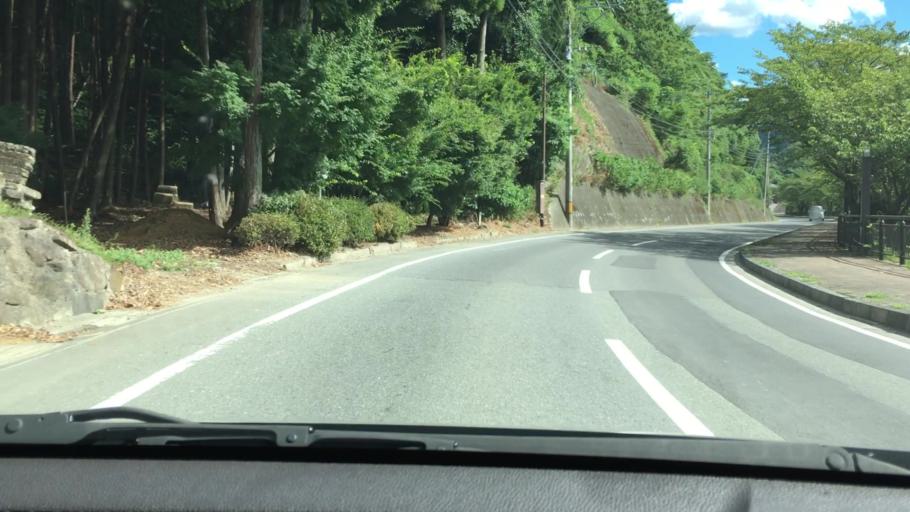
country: JP
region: Saga Prefecture
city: Takeocho-takeo
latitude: 33.1813
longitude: 130.0380
